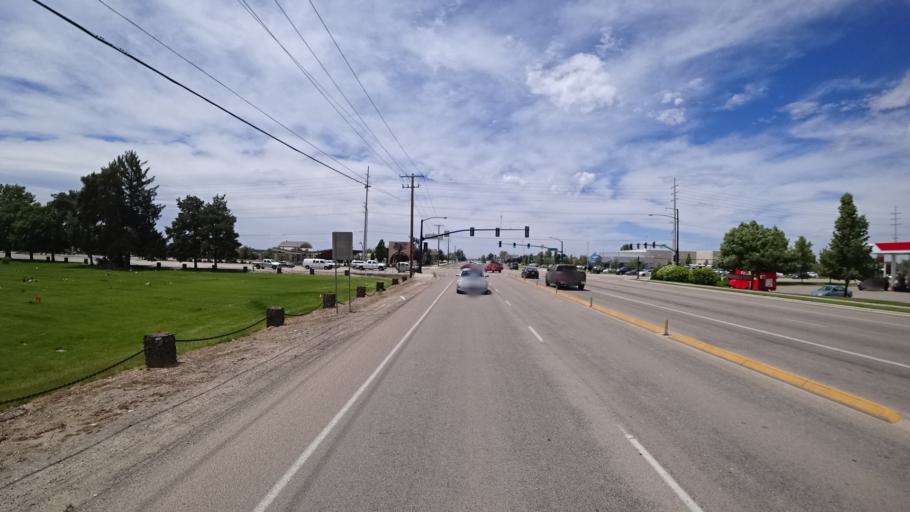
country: US
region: Idaho
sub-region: Ada County
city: Meridian
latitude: 43.6194
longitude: -116.3337
